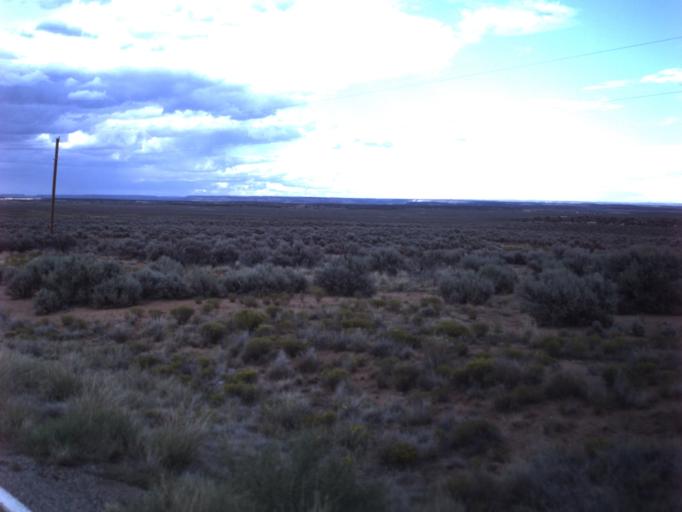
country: US
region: Utah
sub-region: San Juan County
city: Blanding
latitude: 37.3952
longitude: -109.3385
